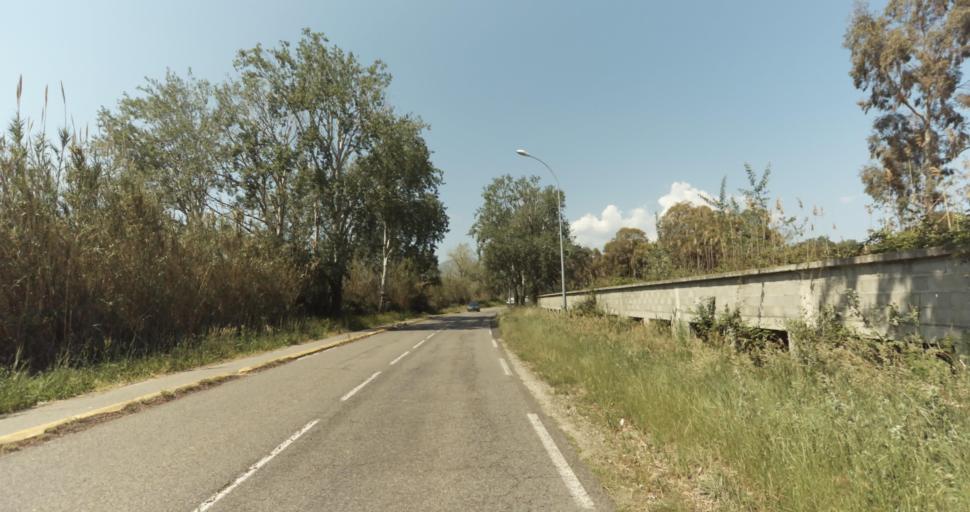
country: FR
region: Corsica
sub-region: Departement de la Haute-Corse
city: Biguglia
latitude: 42.6249
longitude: 9.4700
